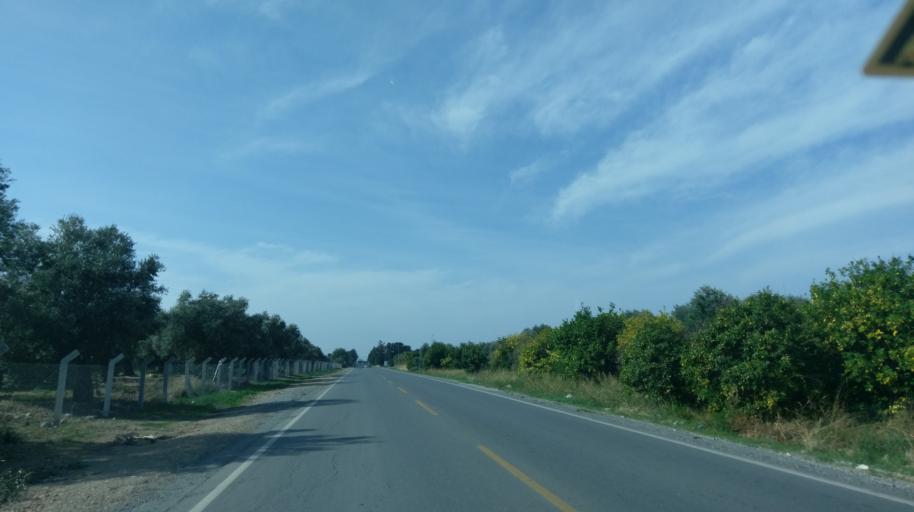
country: CY
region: Keryneia
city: Lapithos
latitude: 35.3524
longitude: 33.1262
